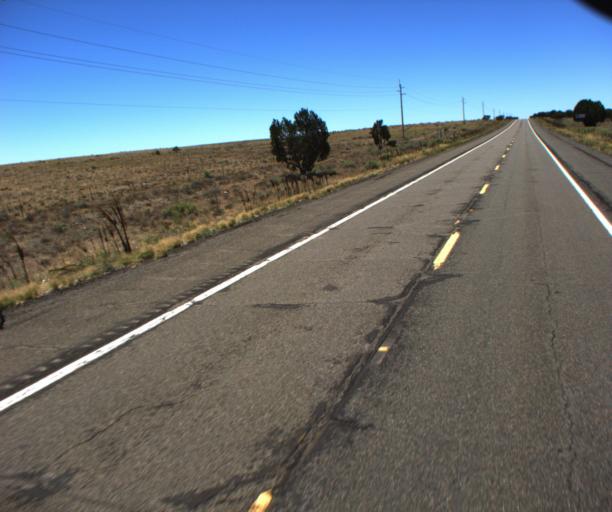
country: US
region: Arizona
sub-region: Coconino County
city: LeChee
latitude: 34.7967
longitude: -110.9850
